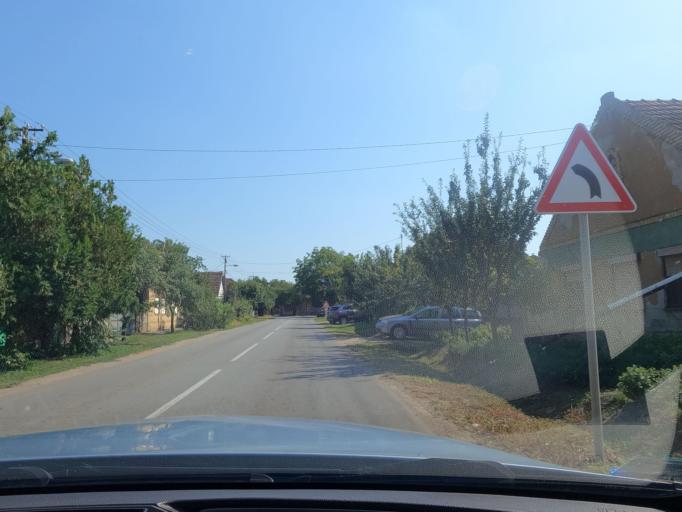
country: RS
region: Autonomna Pokrajina Vojvodina
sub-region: Severnobacki Okrug
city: Backa Topola
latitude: 45.8063
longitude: 19.6453
